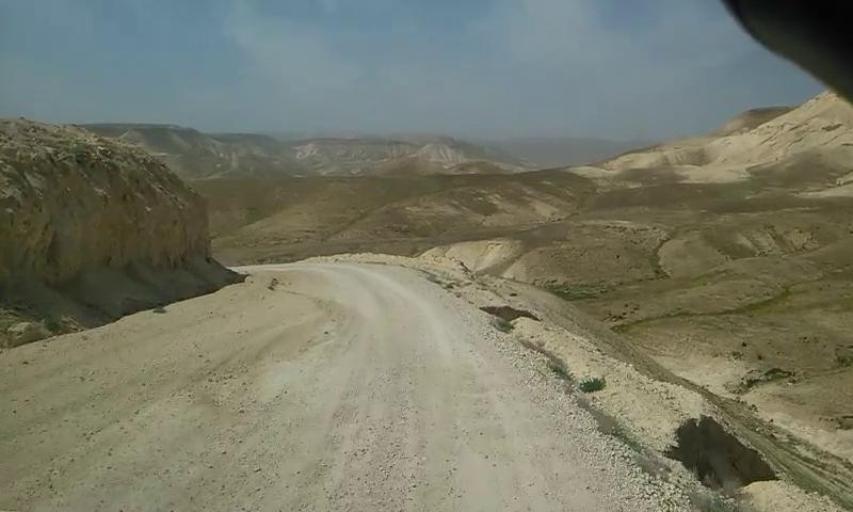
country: PS
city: `Arab ar Rashaydah
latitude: 31.5151
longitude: 35.2856
